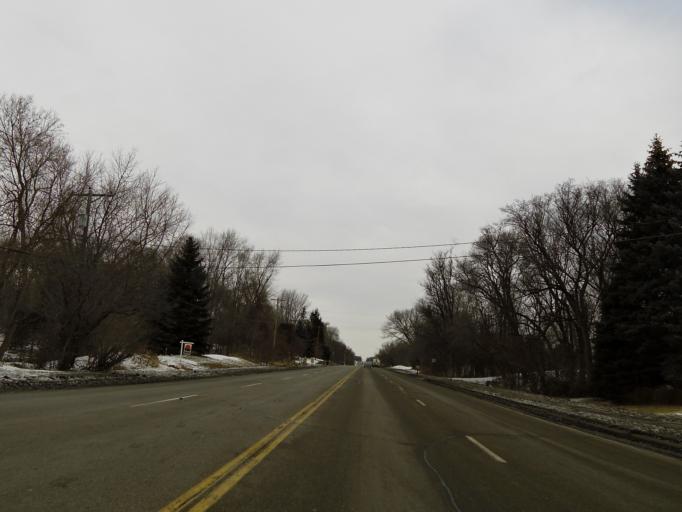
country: US
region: Minnesota
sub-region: Scott County
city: Savage
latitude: 44.8128
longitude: -93.3504
